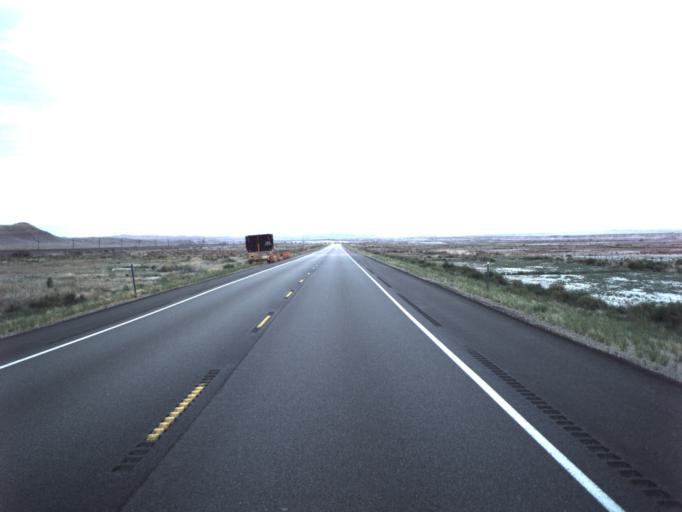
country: US
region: Utah
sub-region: Carbon County
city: East Carbon City
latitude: 39.0127
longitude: -110.2846
